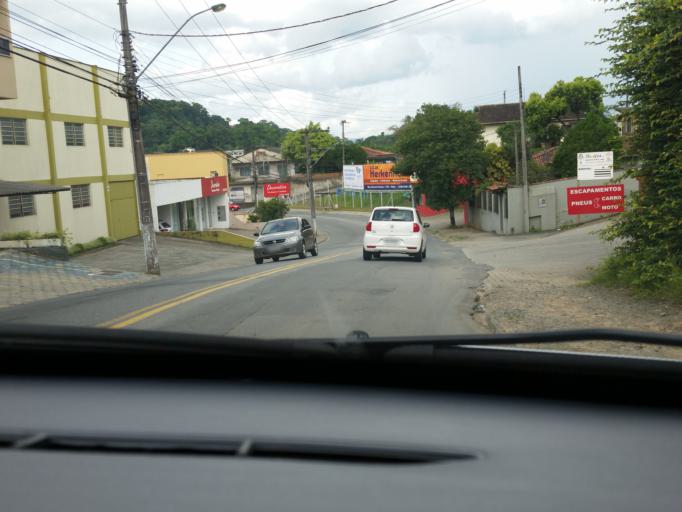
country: BR
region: Santa Catarina
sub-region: Blumenau
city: Blumenau
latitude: -26.9118
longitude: -49.1103
